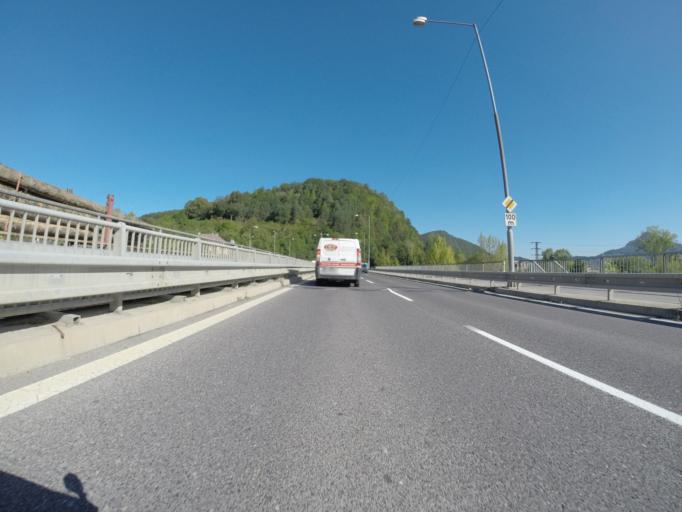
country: SK
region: Trenciansky
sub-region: Okres Povazska Bystrica
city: Povazska Bystrica
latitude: 49.1246
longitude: 18.4386
